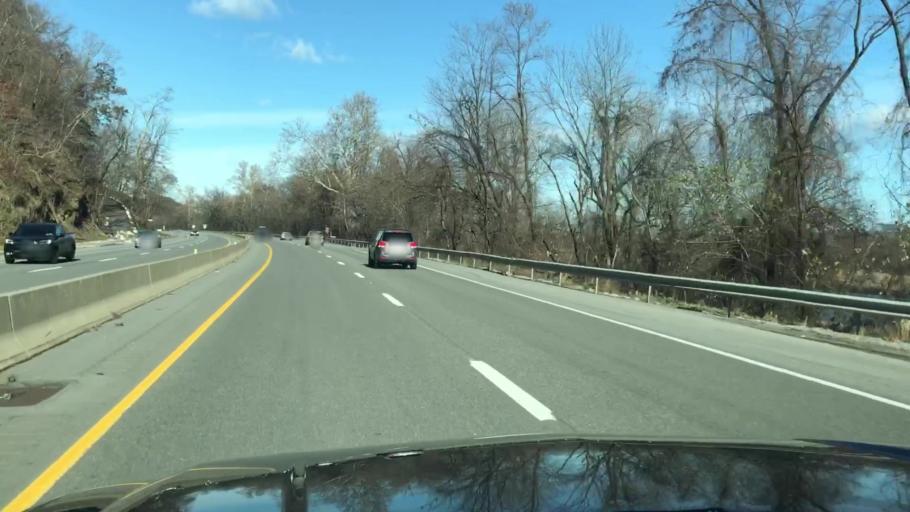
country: US
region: Pennsylvania
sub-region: Snyder County
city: Selinsgrove
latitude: 40.7502
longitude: -76.8588
